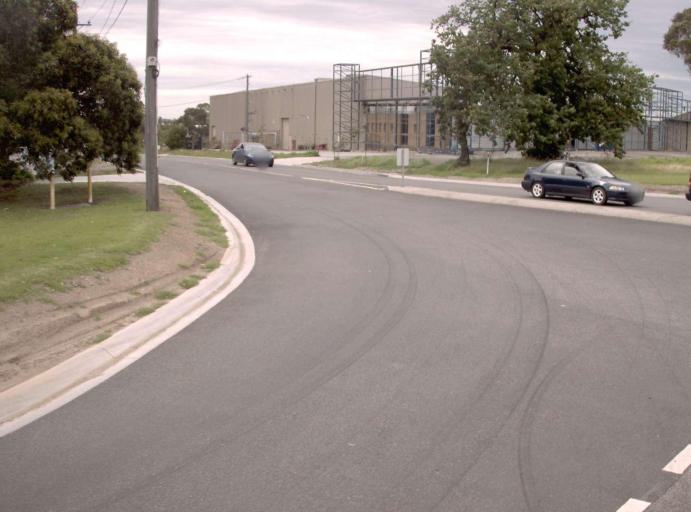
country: AU
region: Victoria
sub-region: Casey
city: Doveton
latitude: -38.0126
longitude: 145.2312
